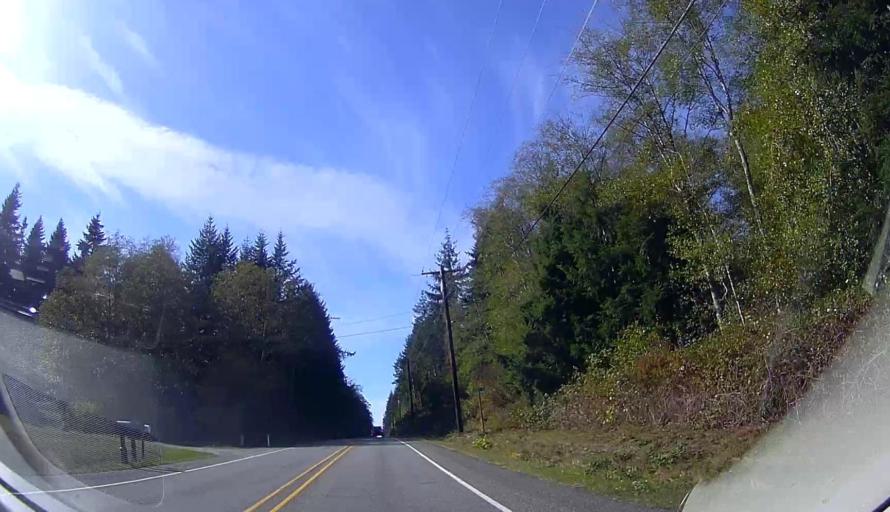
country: US
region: Washington
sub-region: Island County
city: Camano
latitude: 48.2255
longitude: -122.4953
